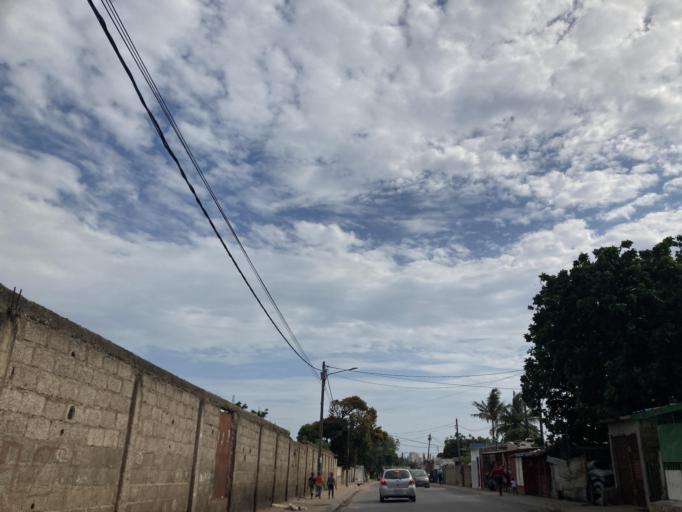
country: MZ
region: Maputo City
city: Maputo
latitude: -25.9356
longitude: 32.5854
